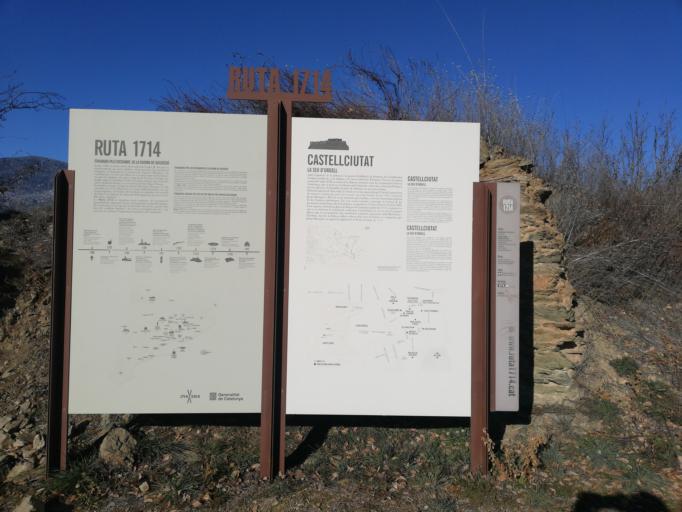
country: ES
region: Catalonia
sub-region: Provincia de Lleida
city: la Seu d'Urgell
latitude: 42.3614
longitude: 1.4494
